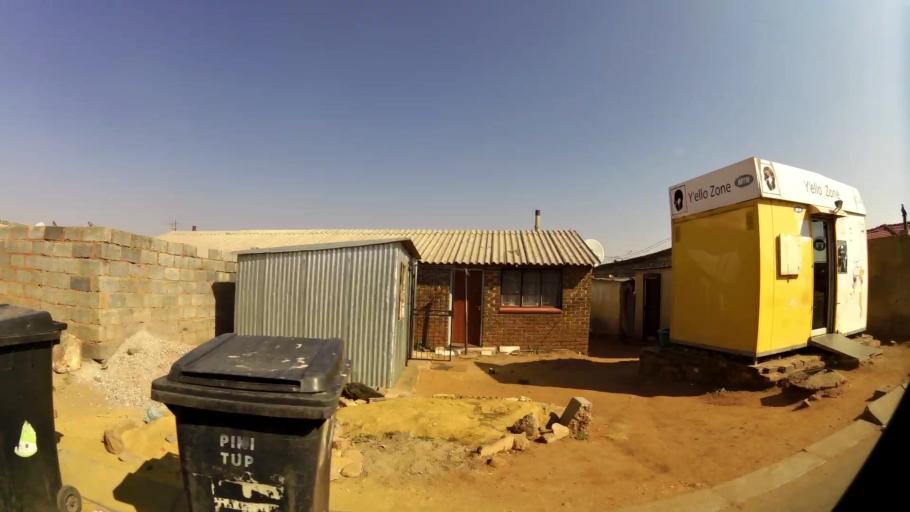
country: ZA
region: Gauteng
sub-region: City of Johannesburg Metropolitan Municipality
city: Soweto
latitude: -26.2477
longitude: 27.9405
